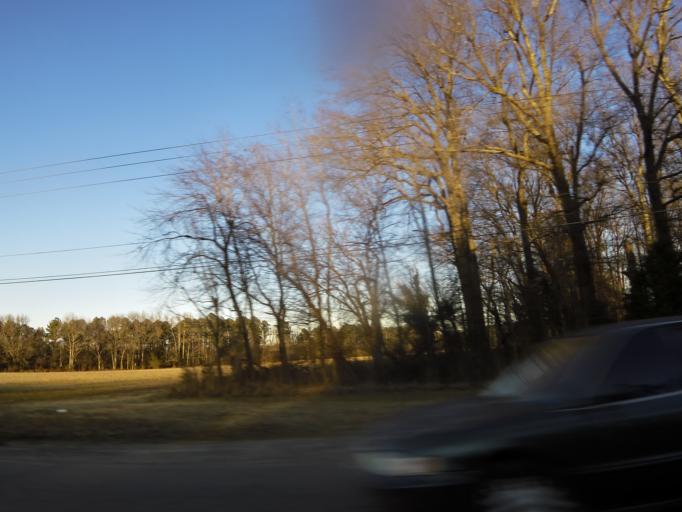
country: US
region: Virginia
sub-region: City of Petersburg
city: Petersburg
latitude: 37.1954
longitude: -77.4268
